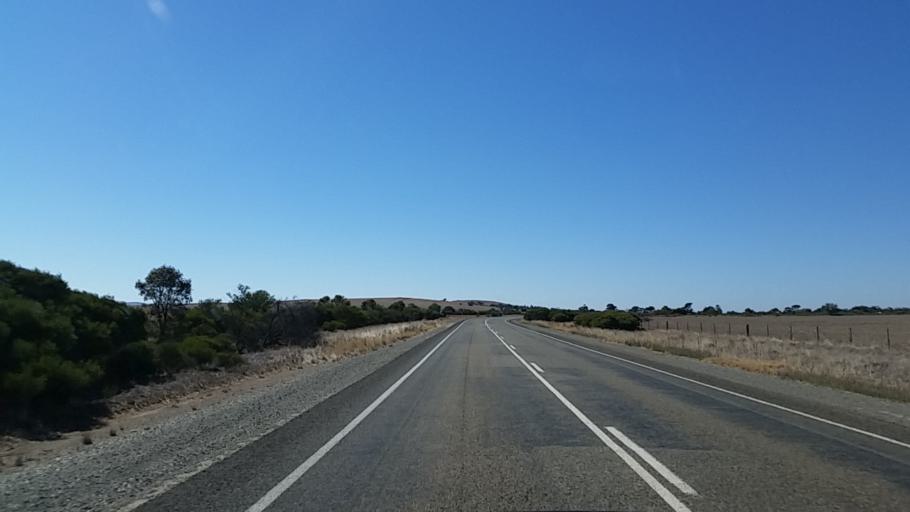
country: AU
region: South Australia
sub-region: Peterborough
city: Peterborough
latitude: -33.2355
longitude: 138.8777
